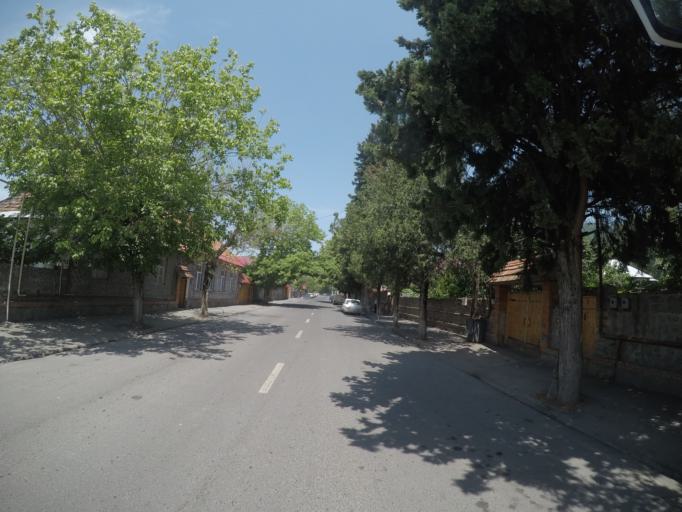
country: AZ
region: Qakh Rayon
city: Qax
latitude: 41.4180
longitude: 46.9189
